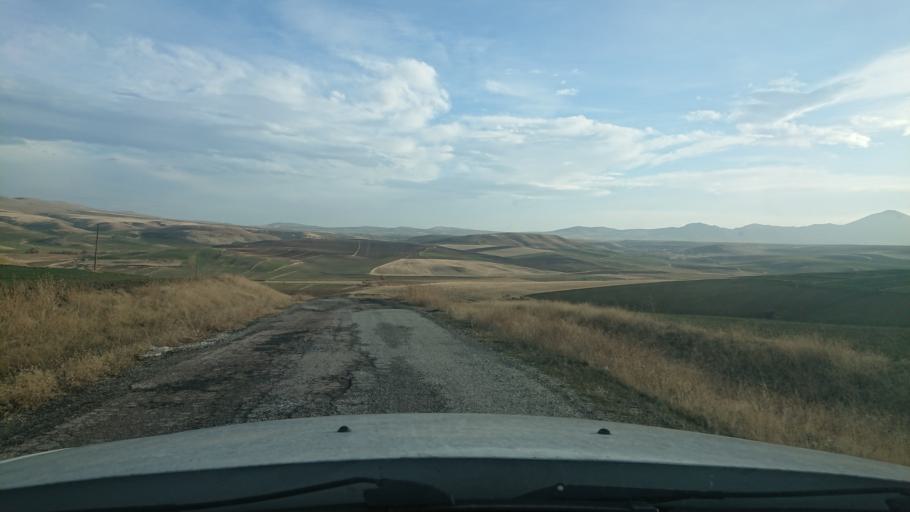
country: TR
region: Aksaray
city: Acipinar
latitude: 38.6704
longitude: 33.8614
